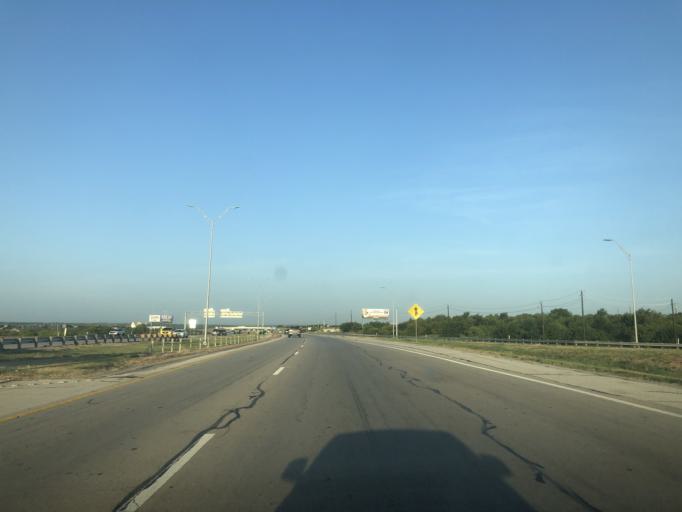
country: US
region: Texas
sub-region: Tarrant County
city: White Settlement
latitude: 32.7375
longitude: -97.4858
